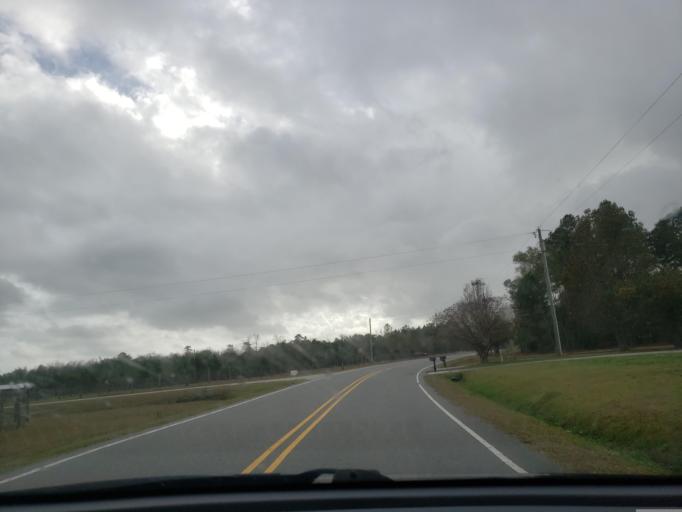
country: US
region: North Carolina
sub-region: Onslow County
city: Richlands
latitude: 34.7334
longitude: -77.6223
